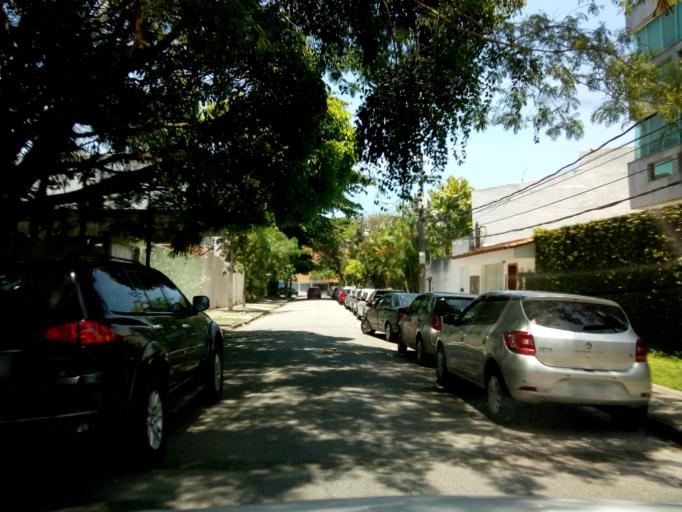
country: BR
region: Rio de Janeiro
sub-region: Rio De Janeiro
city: Rio de Janeiro
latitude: -23.0081
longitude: -43.2941
